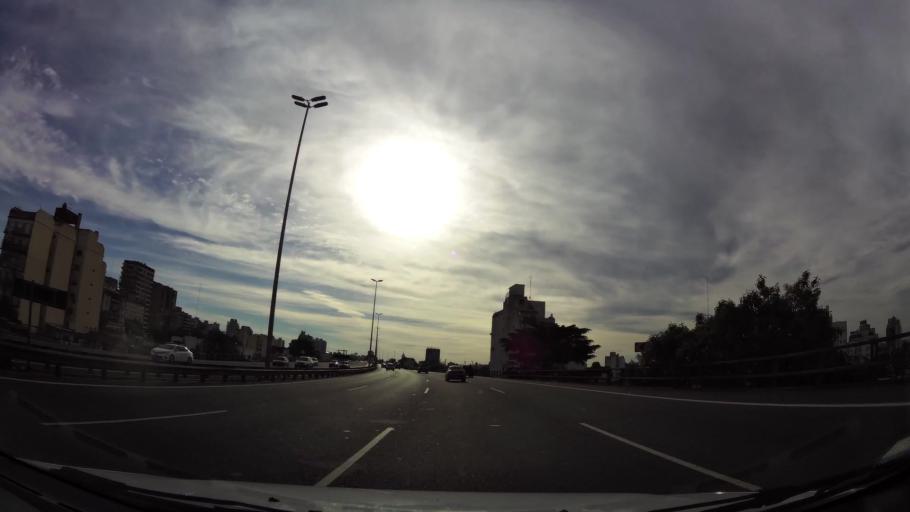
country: AR
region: Buenos Aires F.D.
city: Villa Santa Rita
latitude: -34.6356
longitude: -58.4992
